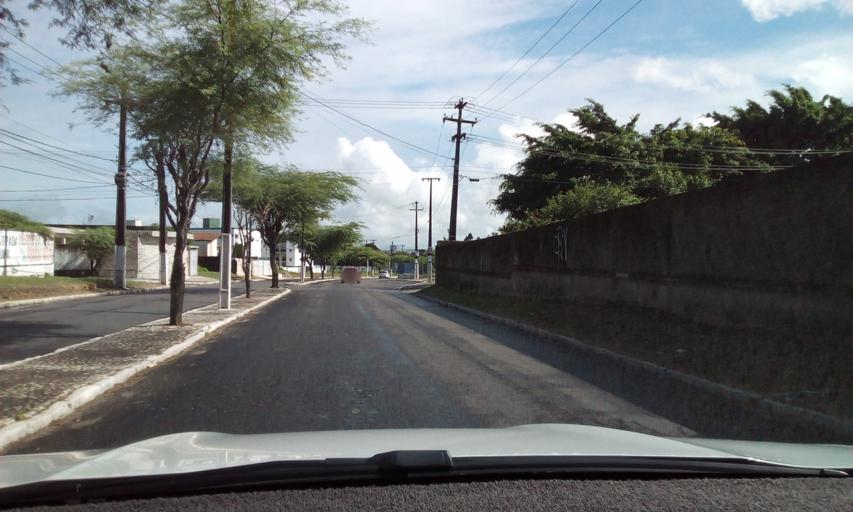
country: BR
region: Paraiba
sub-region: Santa Rita
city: Santa Rita
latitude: -7.1297
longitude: -34.9663
